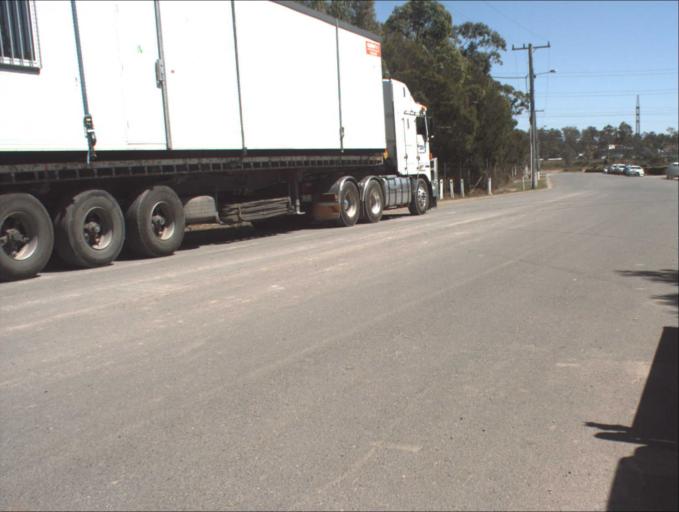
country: AU
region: Queensland
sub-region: Logan
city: Waterford West
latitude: -27.6718
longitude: 153.1164
